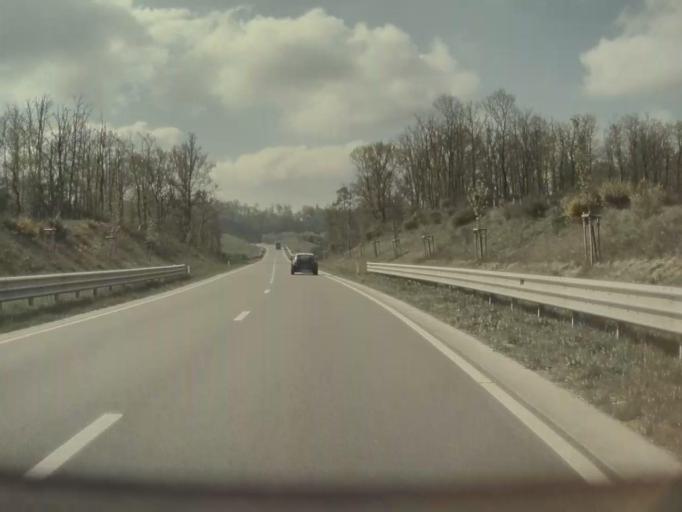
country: BE
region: Wallonia
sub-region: Province du Luxembourg
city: Marche-en-Famenne
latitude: 50.2218
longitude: 5.3145
